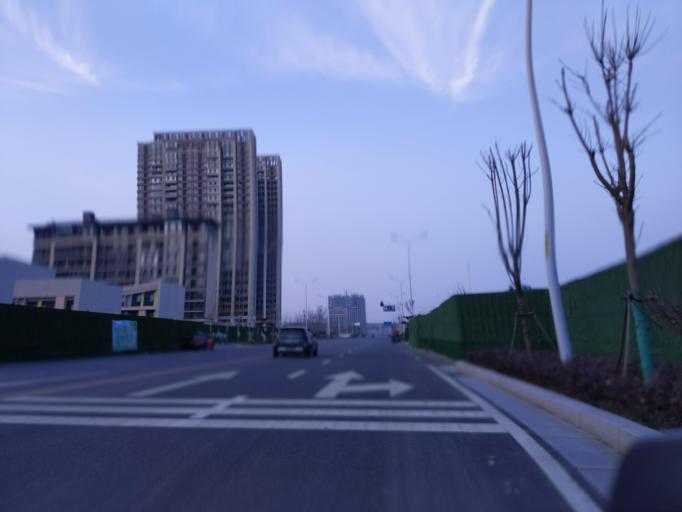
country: CN
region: Henan Sheng
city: Puyang
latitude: 35.8068
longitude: 115.0112
